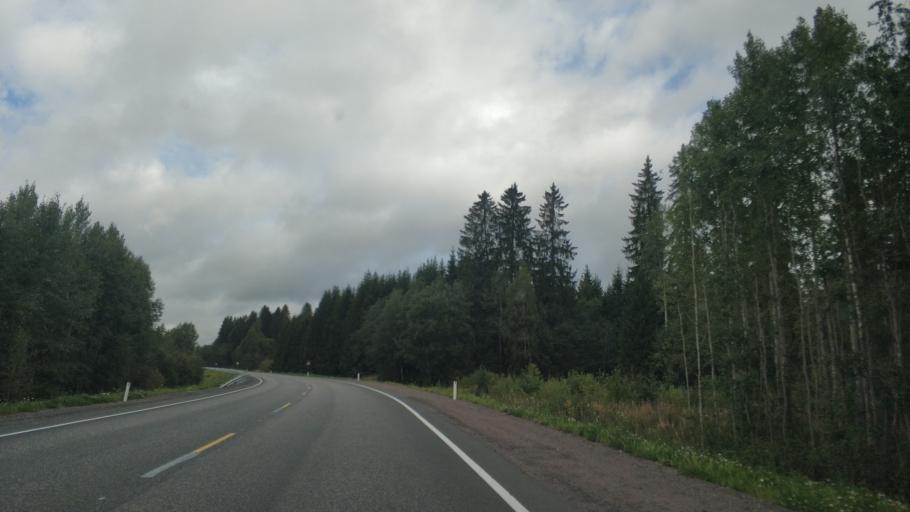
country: RU
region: Republic of Karelia
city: Khelyulya
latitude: 61.7913
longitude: 30.6302
